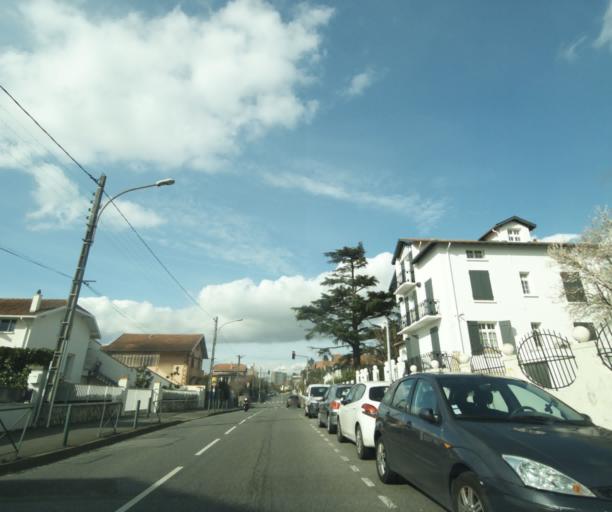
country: FR
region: Midi-Pyrenees
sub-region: Departement de la Haute-Garonne
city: Balma
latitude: 43.5978
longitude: 1.4729
